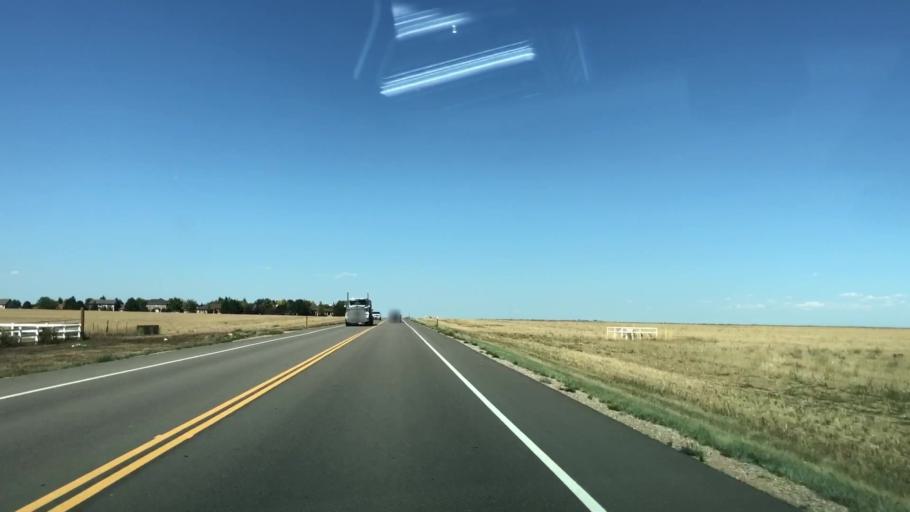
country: US
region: Colorado
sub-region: Weld County
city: Windsor
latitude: 40.4570
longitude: -104.9441
